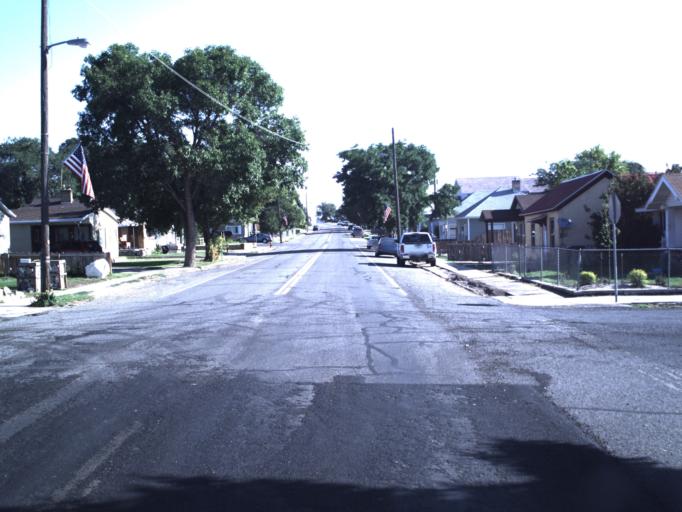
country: US
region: Utah
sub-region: Beaver County
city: Milford
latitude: 38.3979
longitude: -113.0106
